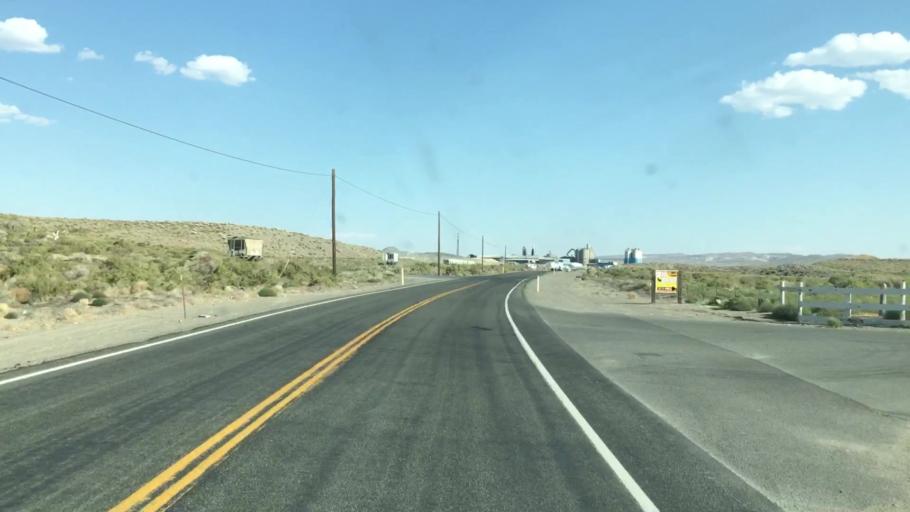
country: US
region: Nevada
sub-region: Lyon County
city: Fernley
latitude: 39.6295
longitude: -119.2763
